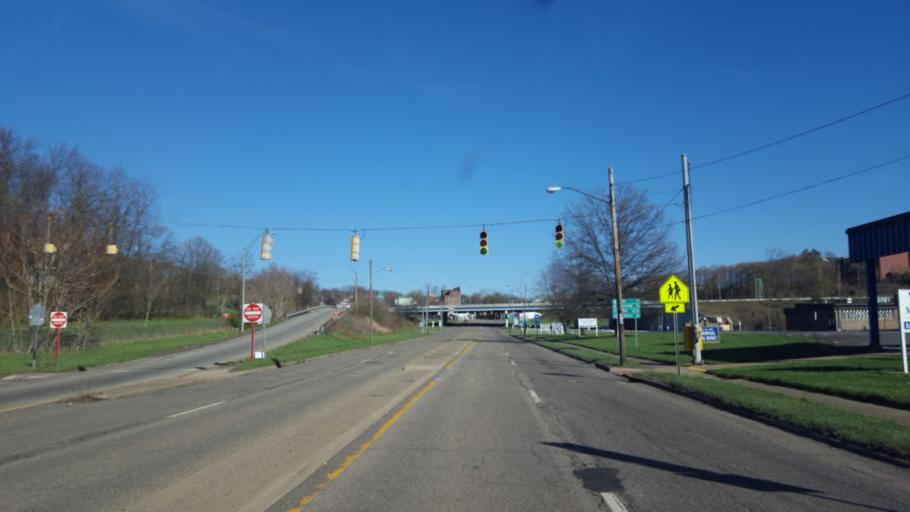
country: US
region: Ohio
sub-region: Columbiana County
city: East Liverpool
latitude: 40.6248
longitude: -80.5890
